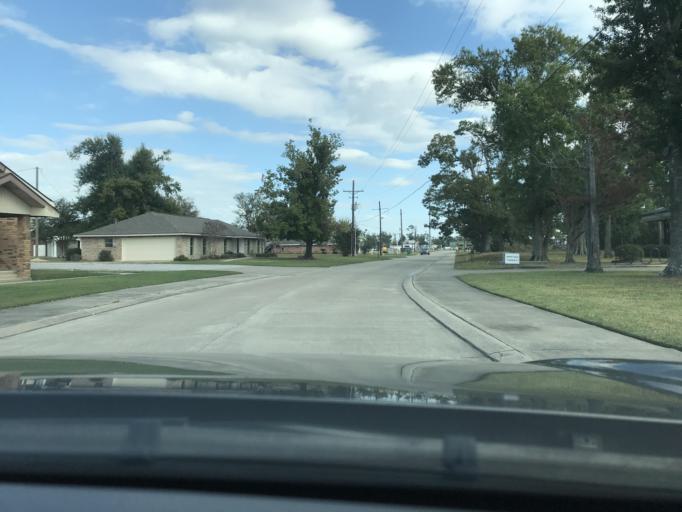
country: US
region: Louisiana
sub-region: Calcasieu Parish
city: Westlake
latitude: 30.2531
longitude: -93.2623
